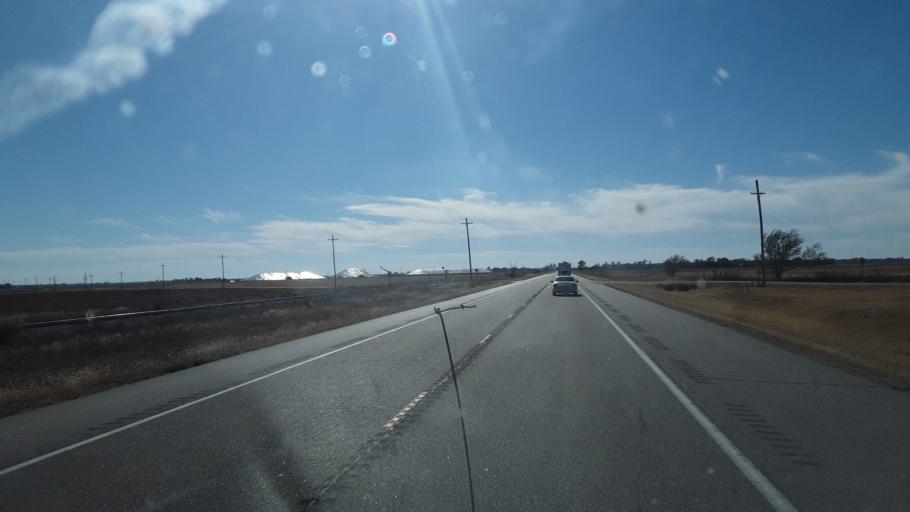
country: US
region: Kansas
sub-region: Pawnee County
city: Larned
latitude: 38.2097
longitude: -99.0581
